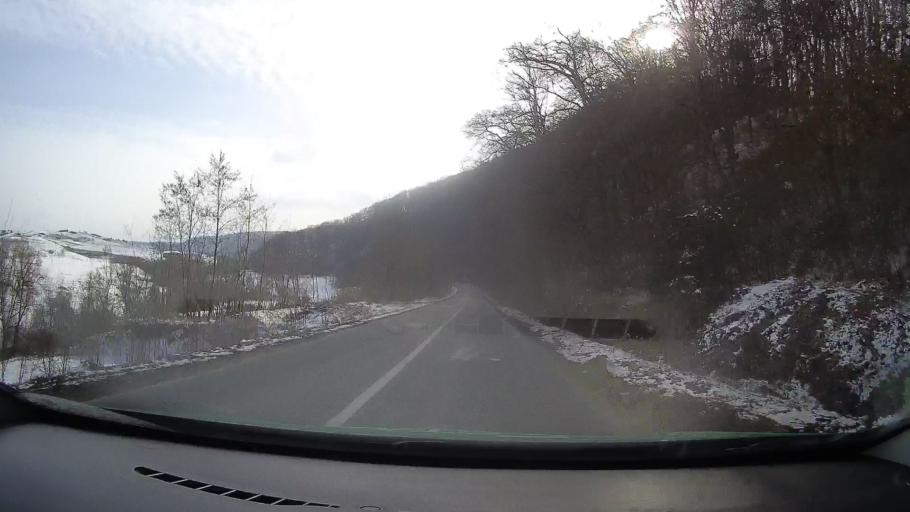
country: RO
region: Mures
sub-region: Comuna Apold
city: Saes
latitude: 46.1743
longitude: 24.7566
